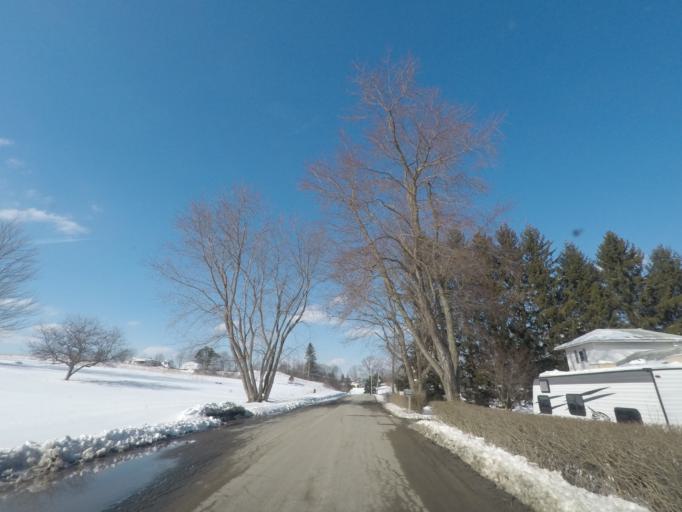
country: US
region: New York
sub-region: Saratoga County
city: Waterford
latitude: 42.7989
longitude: -73.6128
